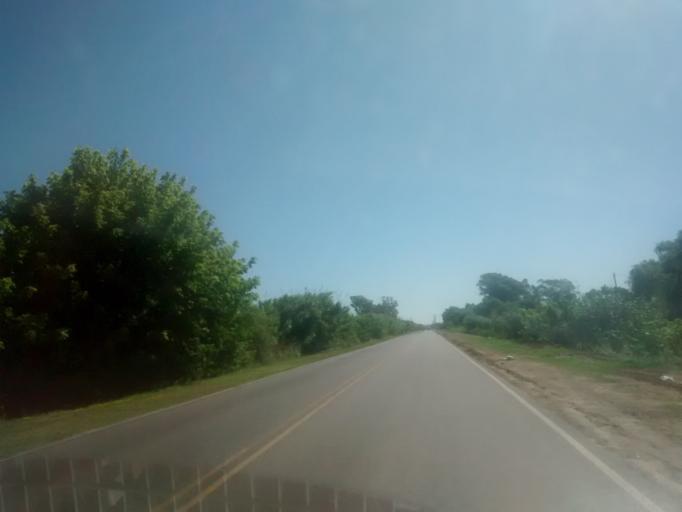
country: AR
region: Buenos Aires
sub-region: Partido de Berisso
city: Berisso
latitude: -34.8821
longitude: -57.8510
